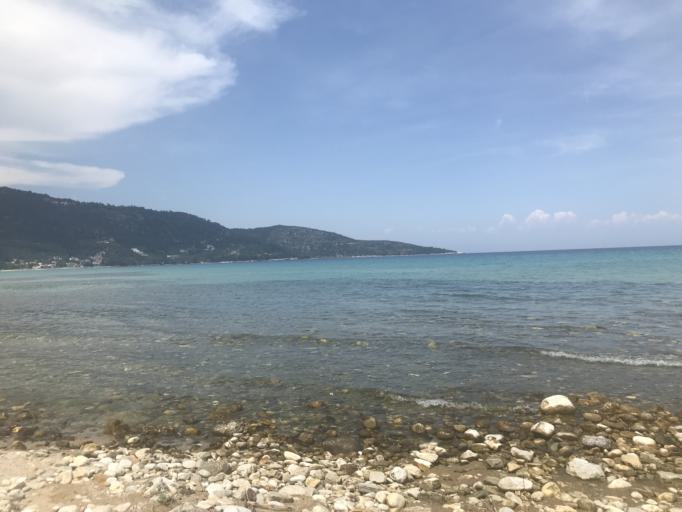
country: GR
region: East Macedonia and Thrace
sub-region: Nomos Kavalas
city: Potamia
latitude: 40.7110
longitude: 24.7591
